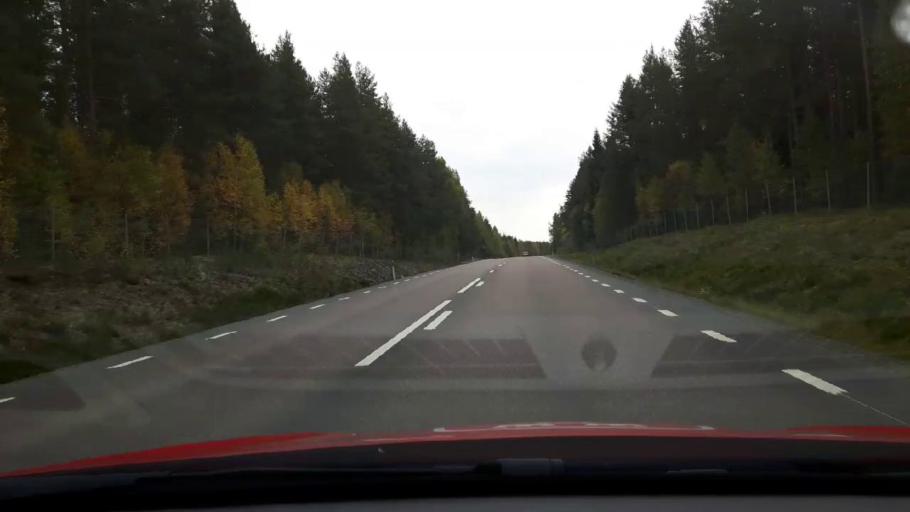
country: SE
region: Gaevleborg
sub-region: Bollnas Kommun
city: Bollnas
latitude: 61.2991
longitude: 16.4797
